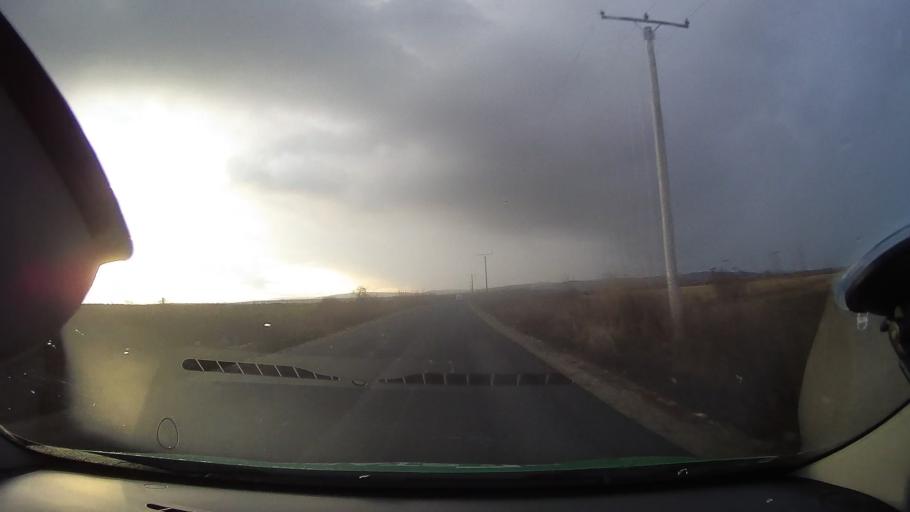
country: RO
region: Cluj
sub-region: Comuna Luna
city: Luncani
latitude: 46.4490
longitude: 23.9391
